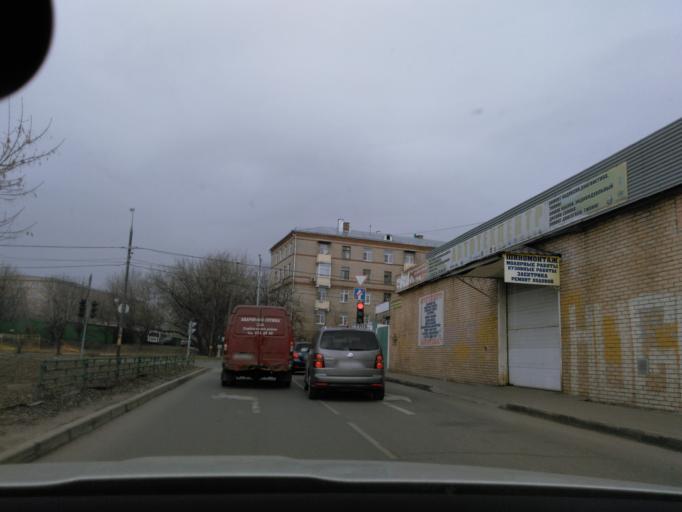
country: RU
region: Moskovskaya
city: Koptevo
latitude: 55.8331
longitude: 37.5209
